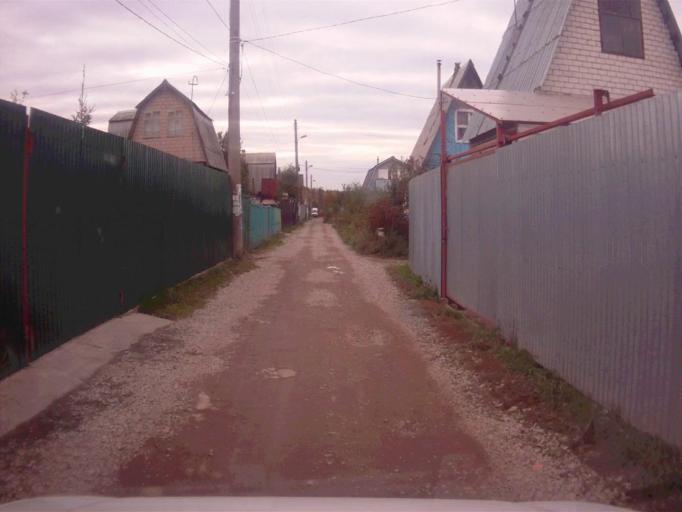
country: RU
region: Chelyabinsk
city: Novosineglazovskiy
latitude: 54.9826
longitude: 61.4058
